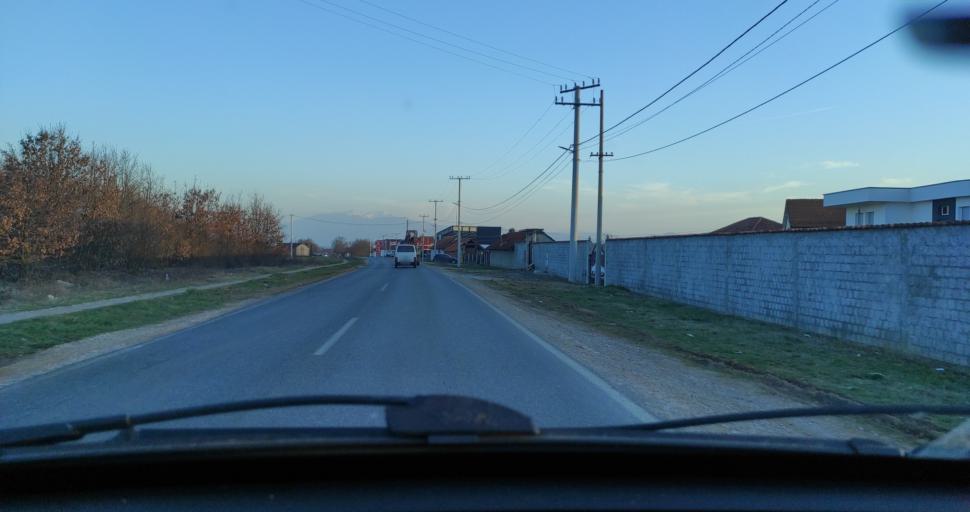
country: XK
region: Gjakova
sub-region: Komuna e Decanit
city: Gllogjan
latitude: 42.4461
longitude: 20.3638
